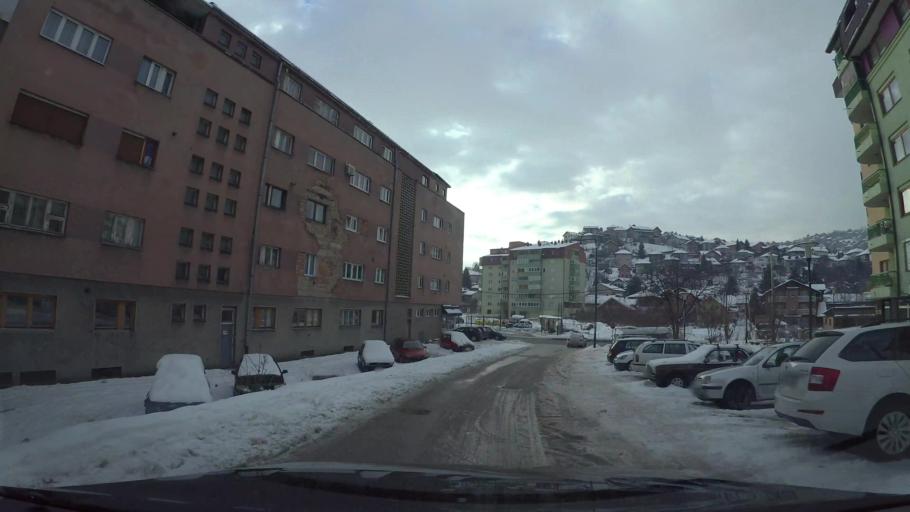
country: BA
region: Federation of Bosnia and Herzegovina
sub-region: Kanton Sarajevo
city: Sarajevo
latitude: 43.8570
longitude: 18.3663
